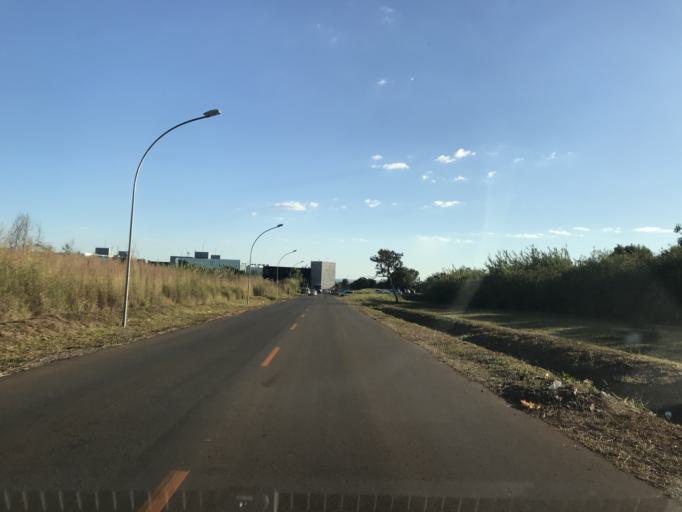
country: BR
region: Federal District
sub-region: Brasilia
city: Brasilia
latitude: -15.8079
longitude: -47.8433
